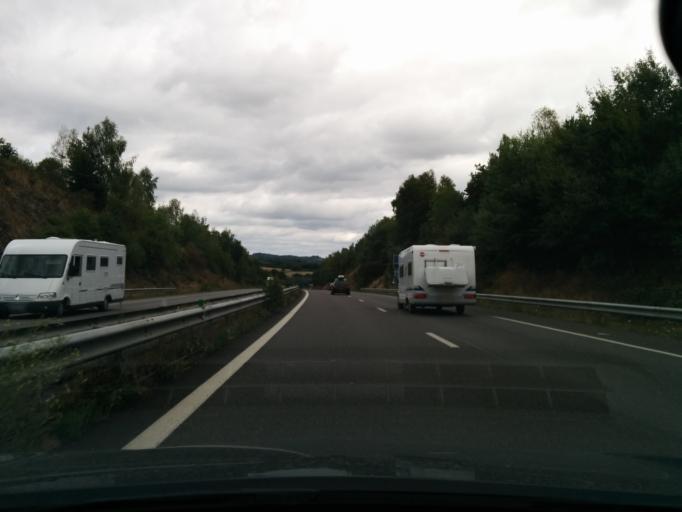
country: FR
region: Limousin
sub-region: Departement de la Haute-Vienne
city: Bessines-sur-Gartempe
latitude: 46.1522
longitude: 1.3778
